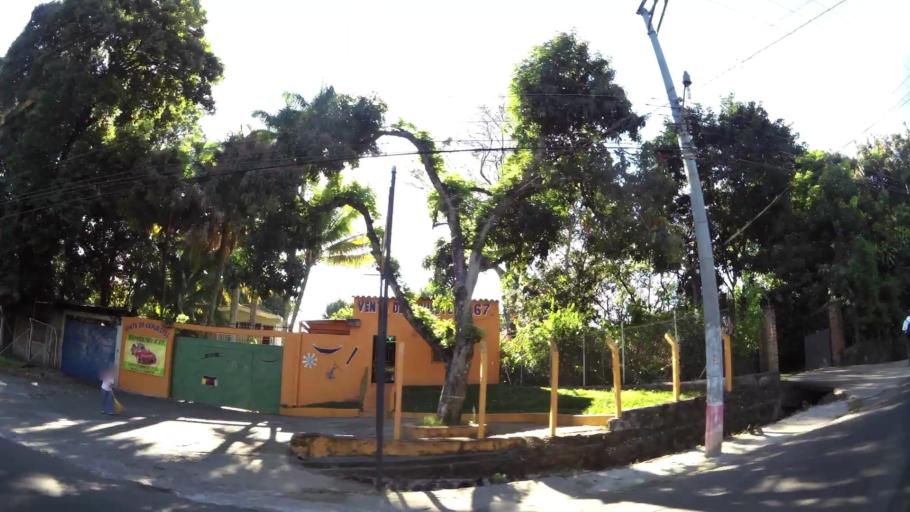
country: SV
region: Santa Ana
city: Santa Ana
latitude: 13.9864
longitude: -89.5679
